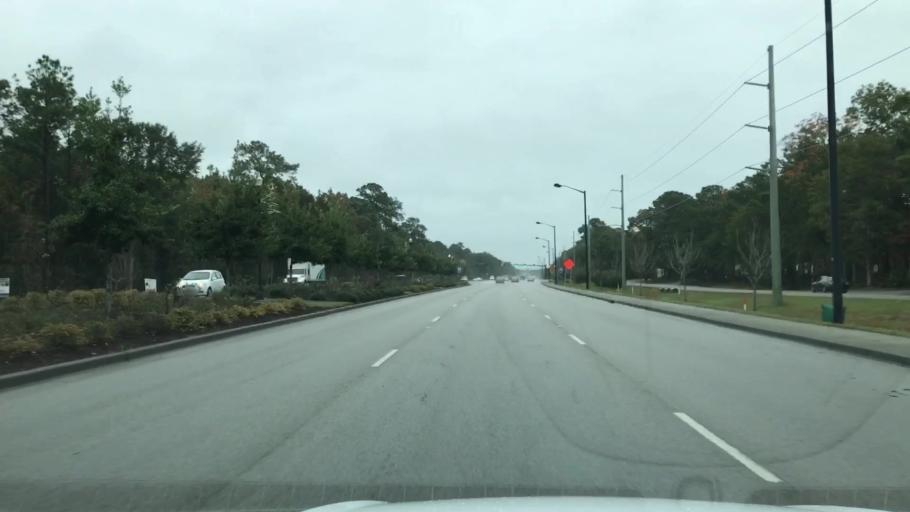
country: US
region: South Carolina
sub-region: Charleston County
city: Isle of Palms
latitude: 32.8735
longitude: -79.7740
